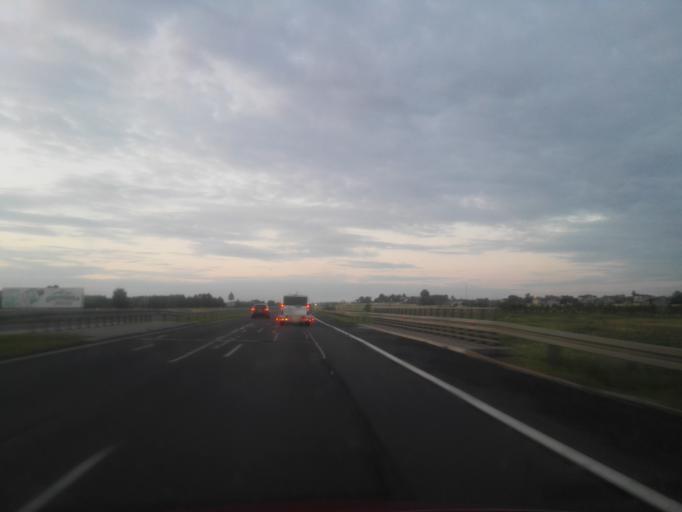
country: PL
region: Lodz Voivodeship
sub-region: Powiat radomszczanski
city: Kamiensk
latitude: 51.2148
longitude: 19.4905
